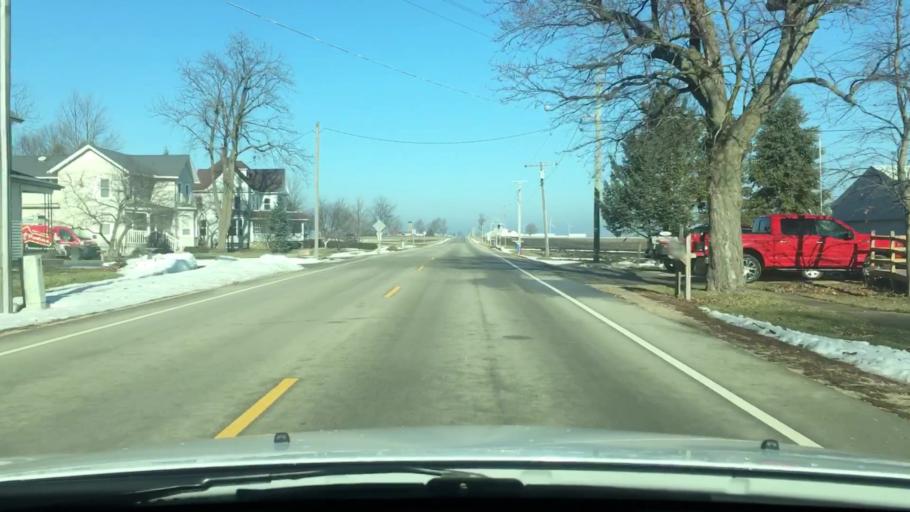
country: US
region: Illinois
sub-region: DeKalb County
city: Waterman
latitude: 41.7698
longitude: -88.8771
